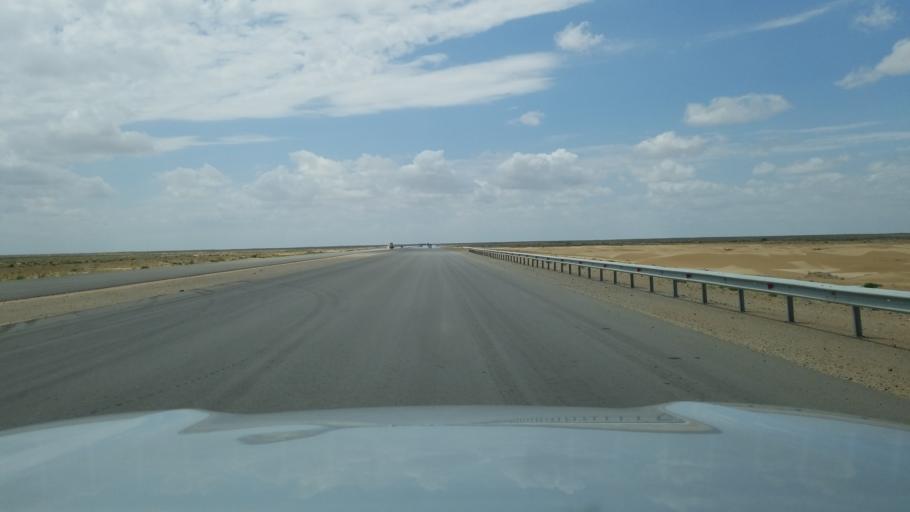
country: TM
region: Balkan
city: Gumdag
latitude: 39.2558
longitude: 54.6431
